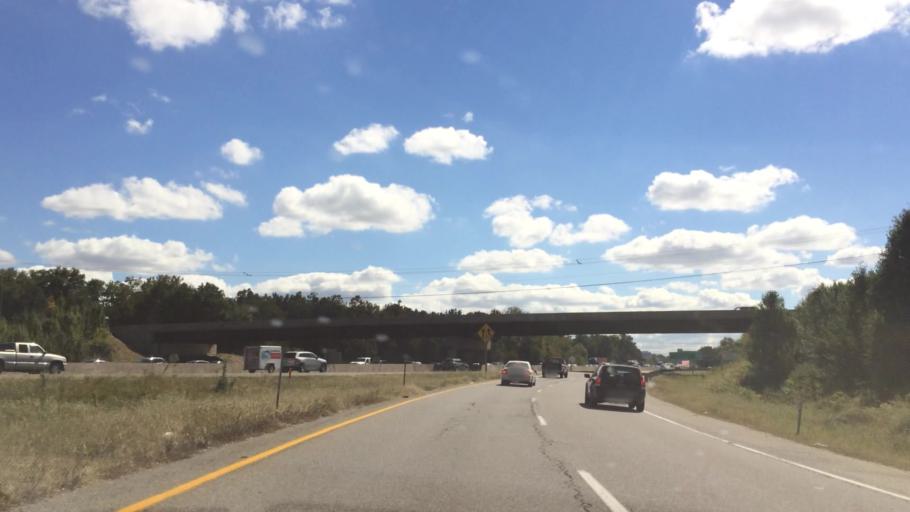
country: US
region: Virginia
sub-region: Henrico County
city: Glen Allen
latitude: 37.6846
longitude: -77.4528
